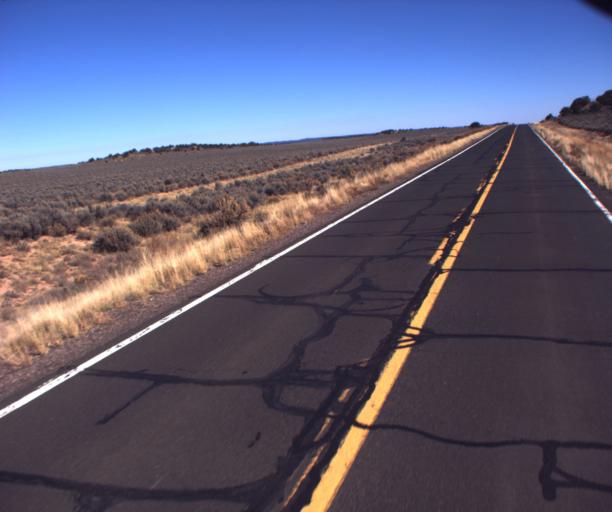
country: US
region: Arizona
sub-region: Navajo County
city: First Mesa
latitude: 35.7450
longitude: -110.0601
